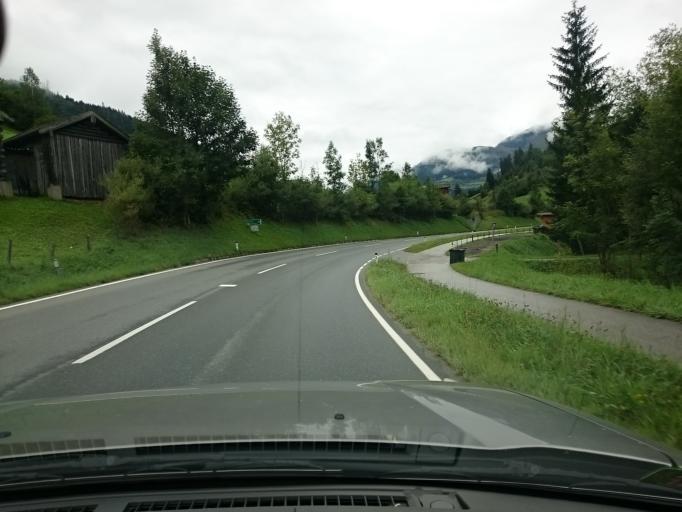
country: AT
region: Salzburg
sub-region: Politischer Bezirk Zell am See
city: Bruck an der Grossglocknerstrasse
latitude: 47.2584
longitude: 12.8246
